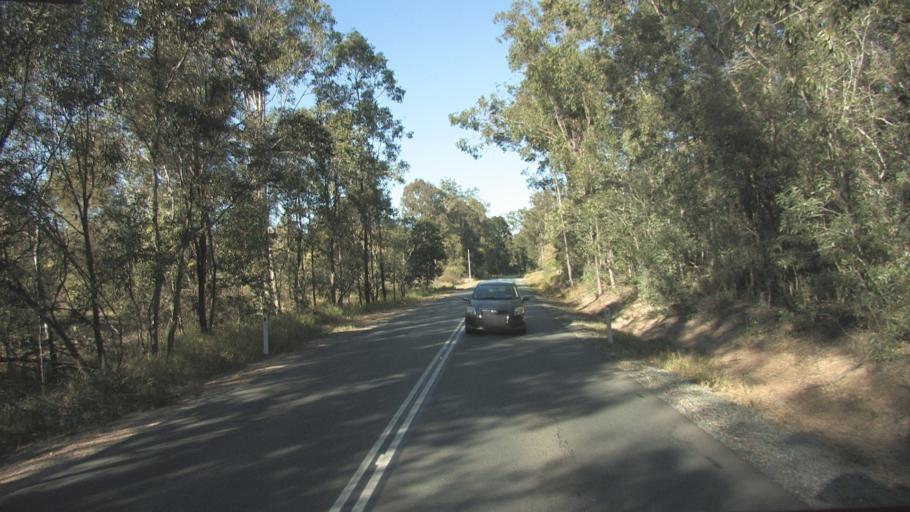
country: AU
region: Queensland
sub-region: Ipswich
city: Springfield Lakes
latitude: -27.7011
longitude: 152.9723
